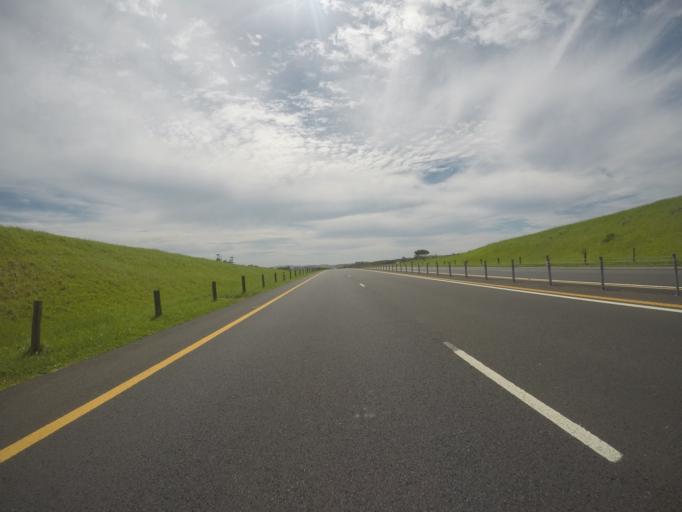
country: ZA
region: KwaZulu-Natal
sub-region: iLembe District Municipality
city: Mandeni
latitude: -29.1842
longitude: 31.4831
